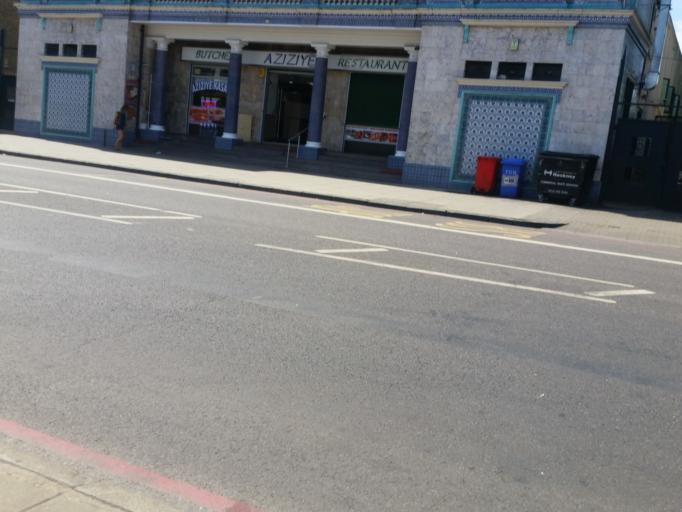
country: GB
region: England
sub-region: Greater London
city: Hackney
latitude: 51.5554
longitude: -0.0745
